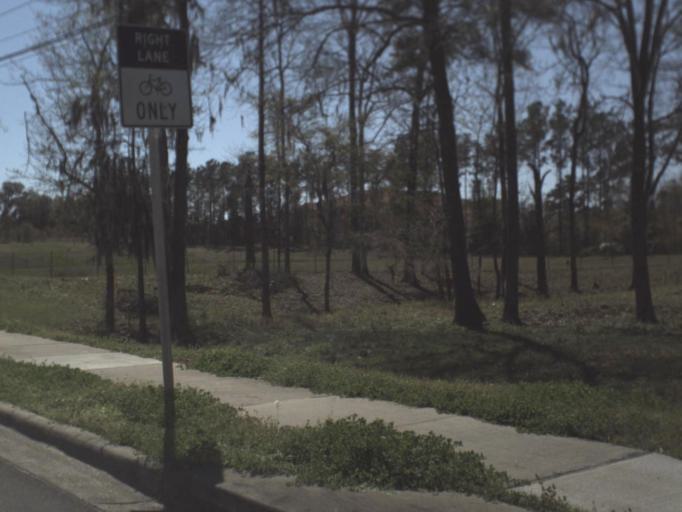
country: US
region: Florida
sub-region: Leon County
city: Tallahassee
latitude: 30.4758
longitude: -84.3634
